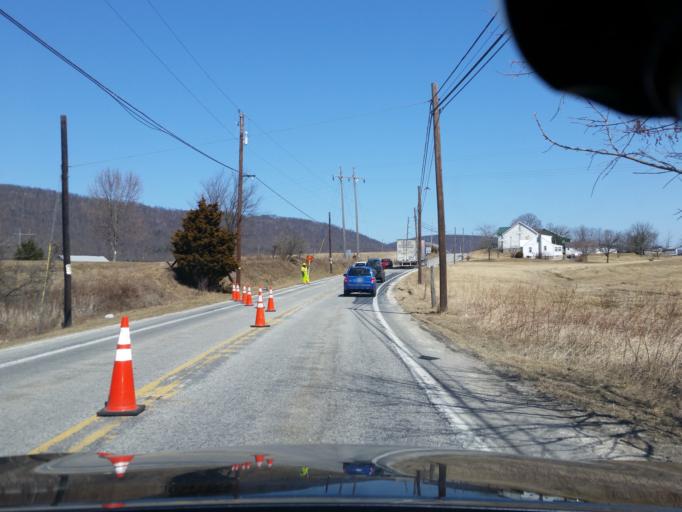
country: US
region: Pennsylvania
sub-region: Cumberland County
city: Schlusser
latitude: 40.2728
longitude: -77.1622
